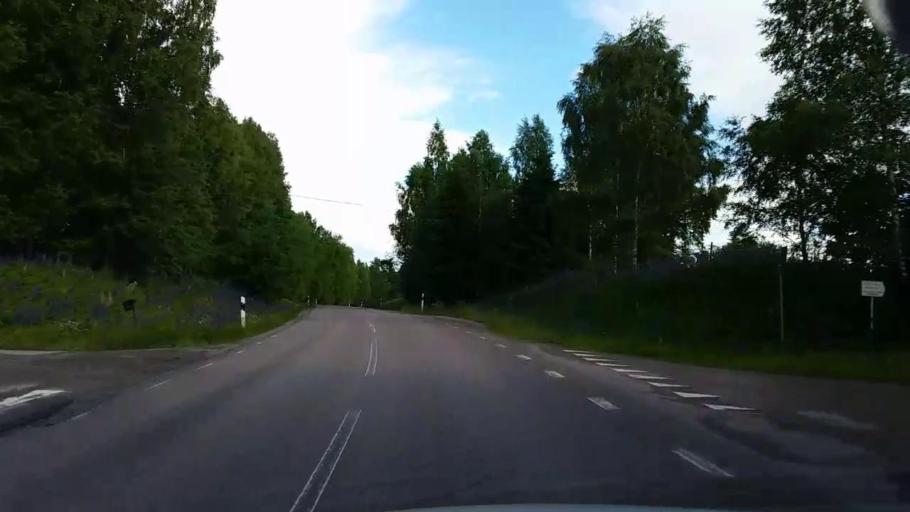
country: SE
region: Vaestmanland
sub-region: Fagersta Kommun
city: Fagersta
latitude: 59.9526
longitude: 15.7871
